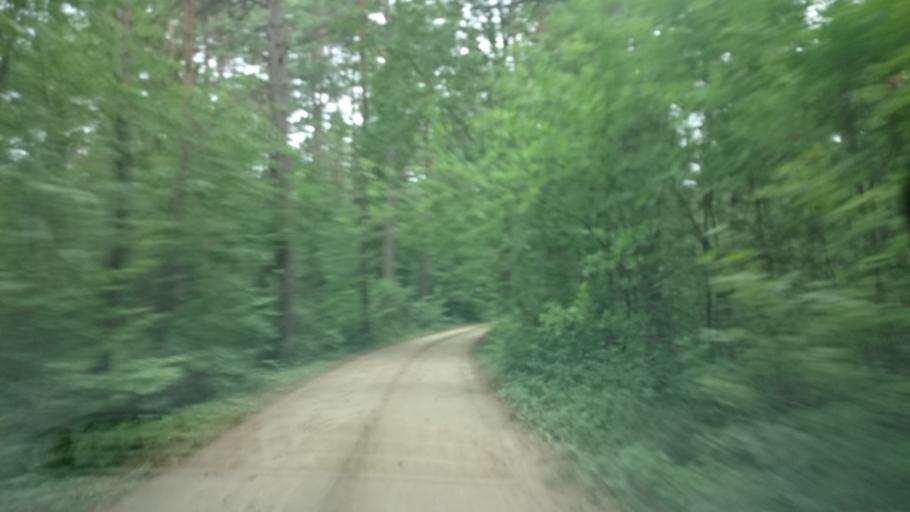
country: EE
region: Saare
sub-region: Orissaare vald
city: Orissaare
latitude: 58.5954
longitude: 22.6966
